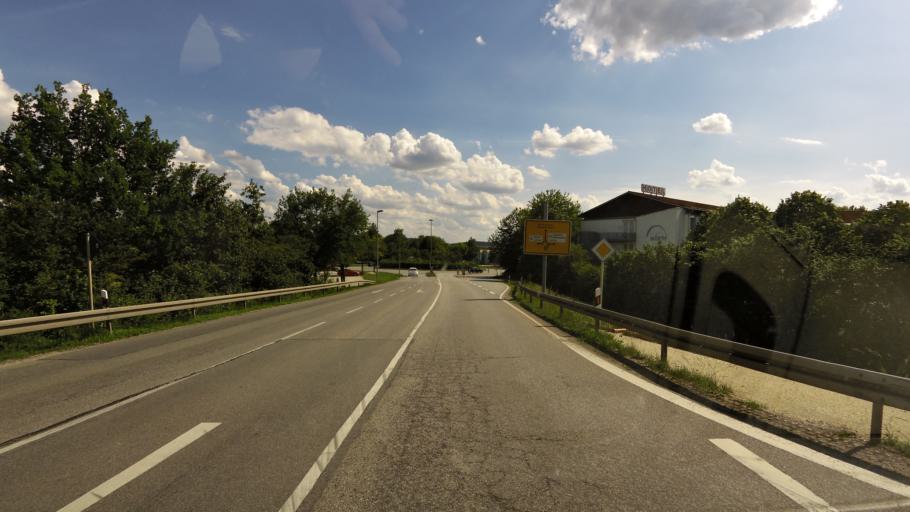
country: DE
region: Bavaria
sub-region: Lower Bavaria
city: Worth an der Isar
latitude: 48.6266
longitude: 12.3217
